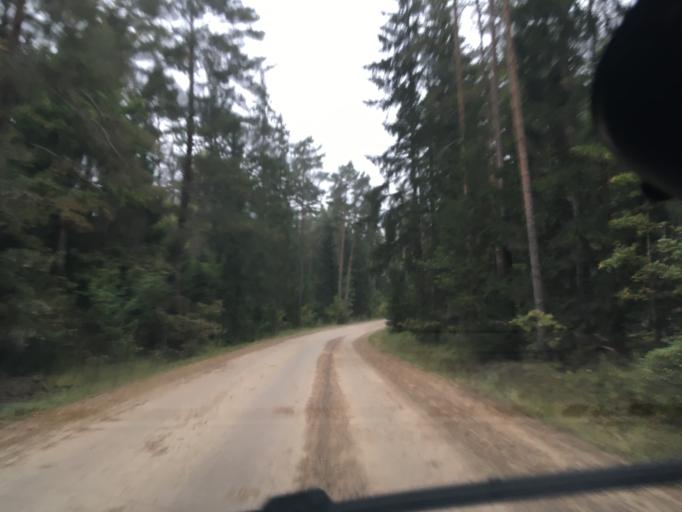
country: LV
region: Kuldigas Rajons
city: Kuldiga
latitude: 56.9905
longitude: 21.9741
